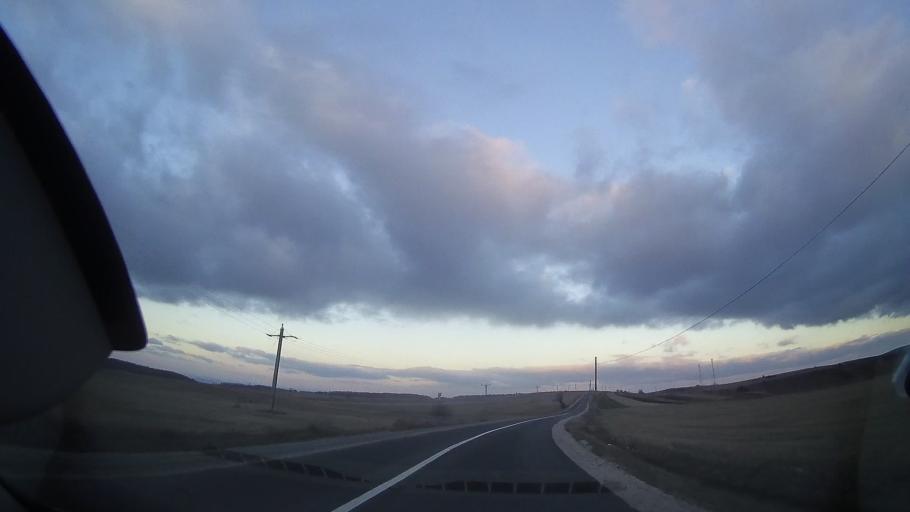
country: RO
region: Cluj
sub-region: Comuna Izvoru Crisului
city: Izvoru Crisului
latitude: 46.8160
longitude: 23.1397
